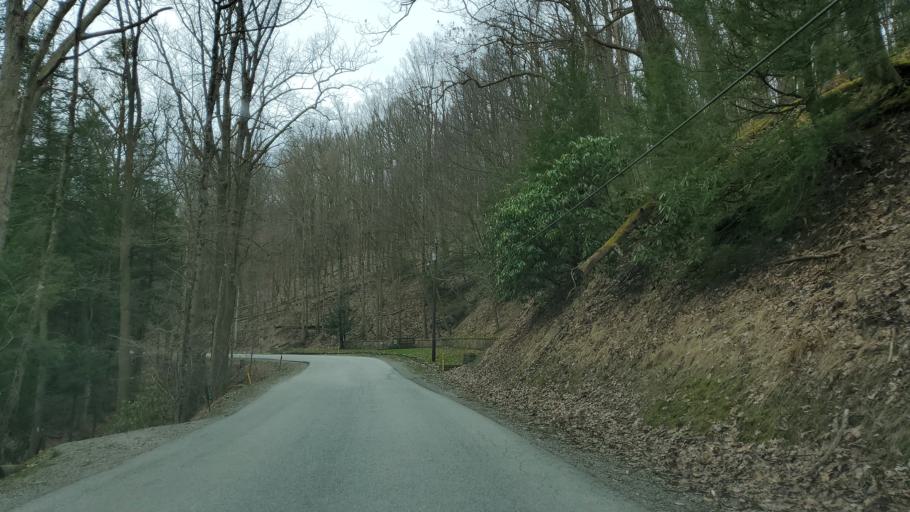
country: US
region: Pennsylvania
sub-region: Westmoreland County
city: Ligonier
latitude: 40.1723
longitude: -79.2361
